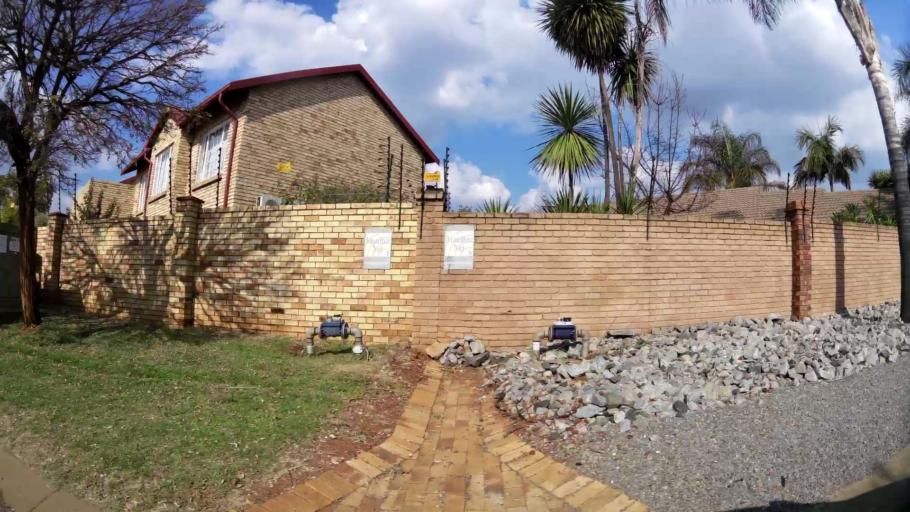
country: ZA
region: Gauteng
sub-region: City of Tshwane Metropolitan Municipality
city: Centurion
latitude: -25.8761
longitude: 28.1945
